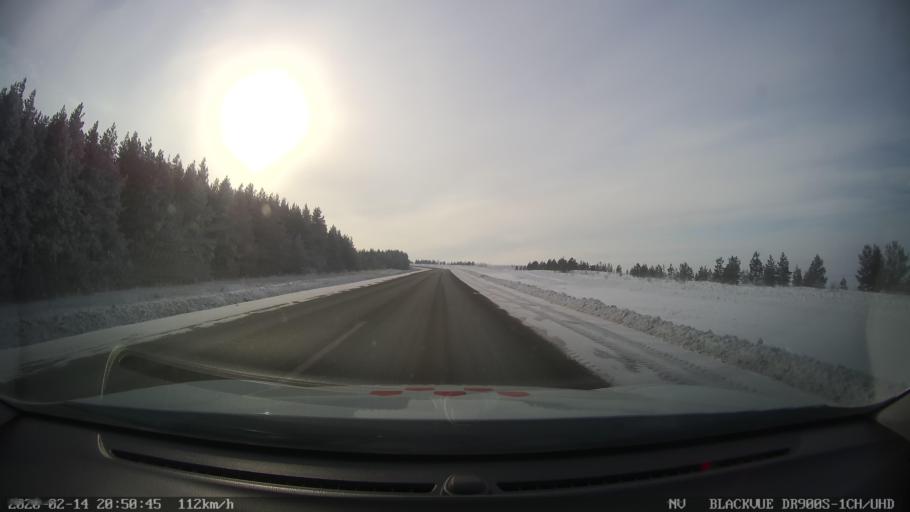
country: RU
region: Tatarstan
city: Kuybyshevskiy Zaton
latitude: 55.2224
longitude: 49.2323
